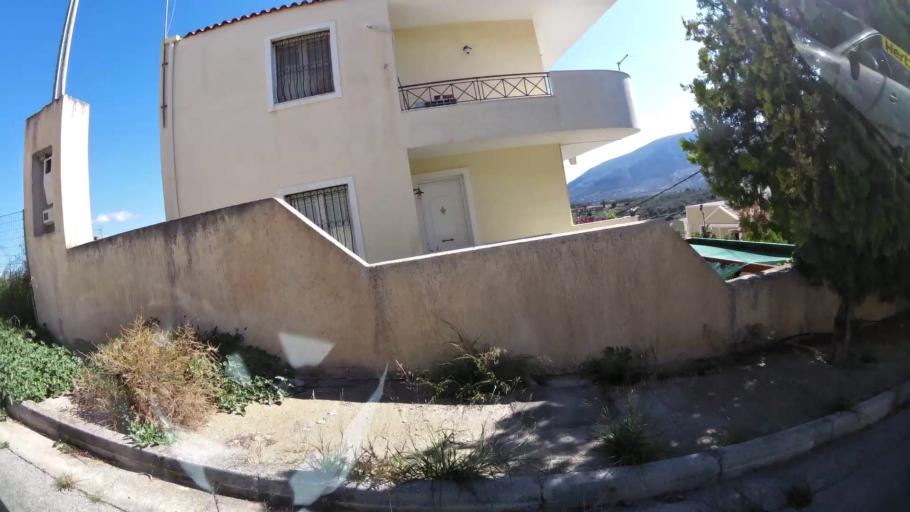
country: GR
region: Attica
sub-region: Nomarchia Anatolikis Attikis
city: Markopoulo
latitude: 37.8853
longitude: 23.9419
